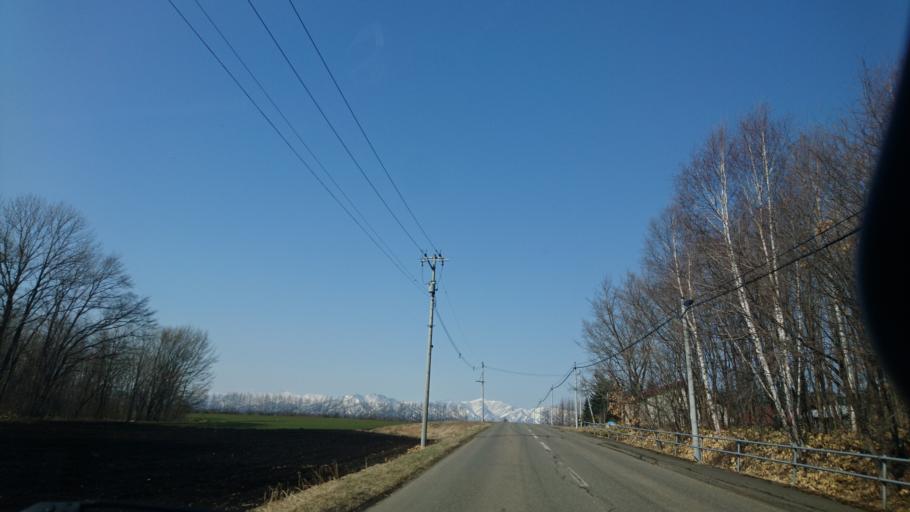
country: JP
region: Hokkaido
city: Obihiro
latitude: 42.9048
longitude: 143.1038
